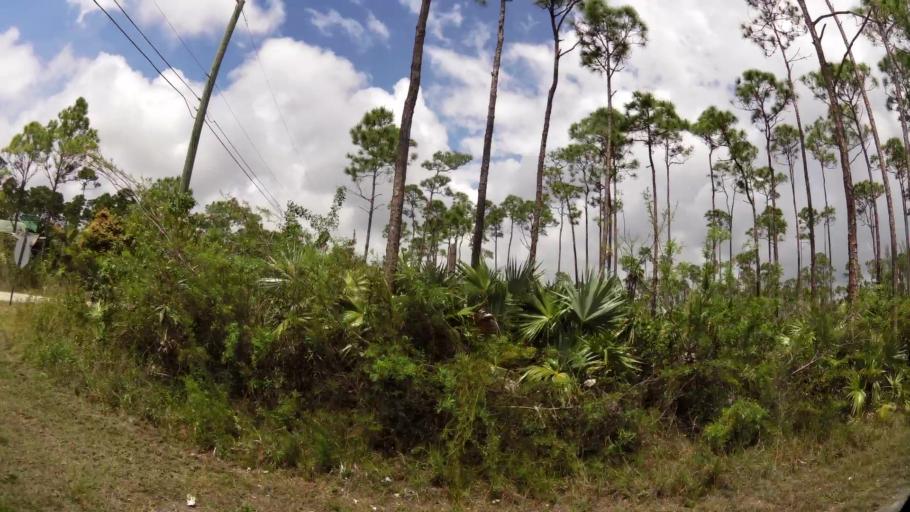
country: BS
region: Freeport
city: Lucaya
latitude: 26.5348
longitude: -78.6478
